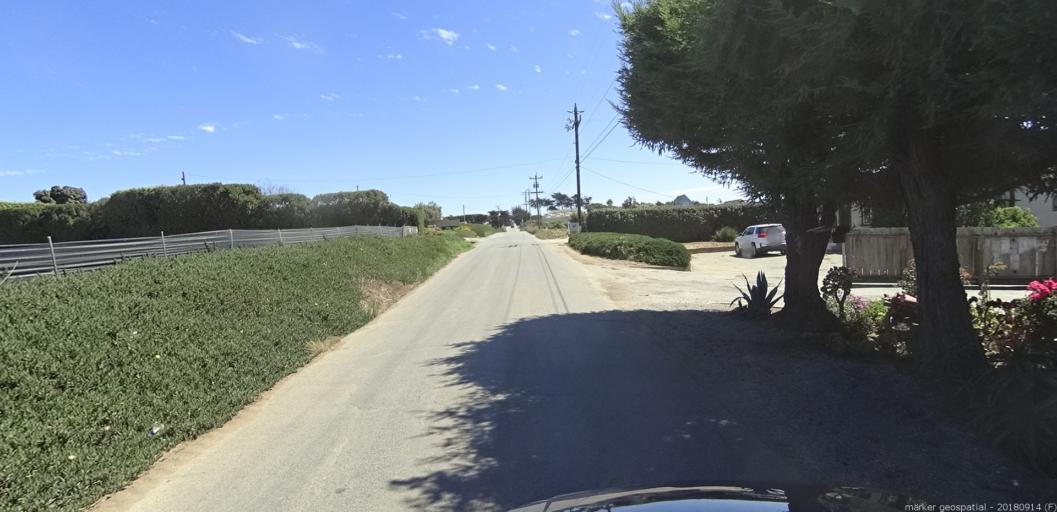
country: US
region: California
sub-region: Monterey County
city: Las Lomas
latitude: 36.8559
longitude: -121.7951
